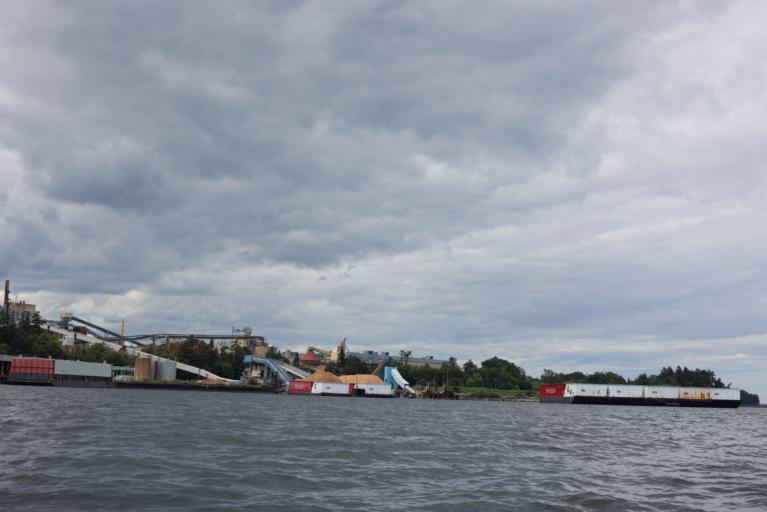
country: CA
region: British Columbia
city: North Cowichan
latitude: 48.8722
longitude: -123.6360
